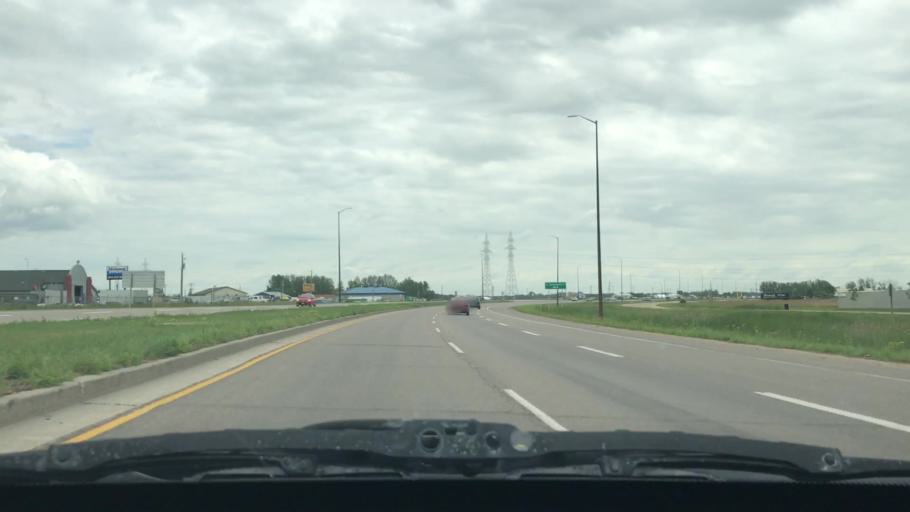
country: CA
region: Manitoba
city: Winnipeg
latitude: 49.8555
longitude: -97.0109
